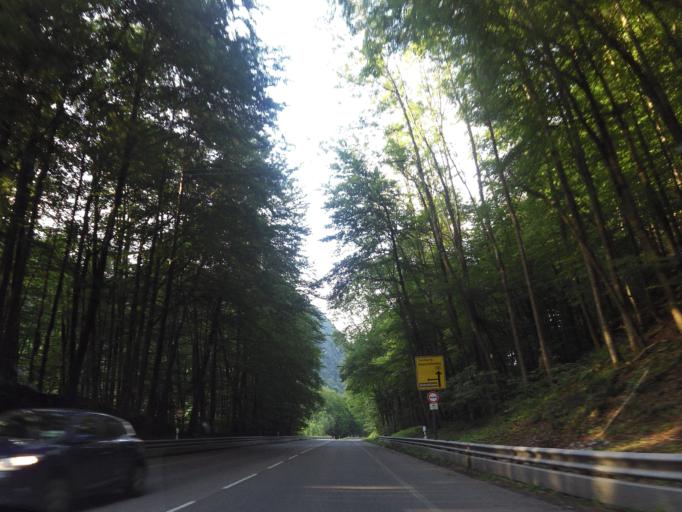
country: DE
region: Bavaria
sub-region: Upper Bavaria
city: Marktschellenberg
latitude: 47.6688
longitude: 13.0352
